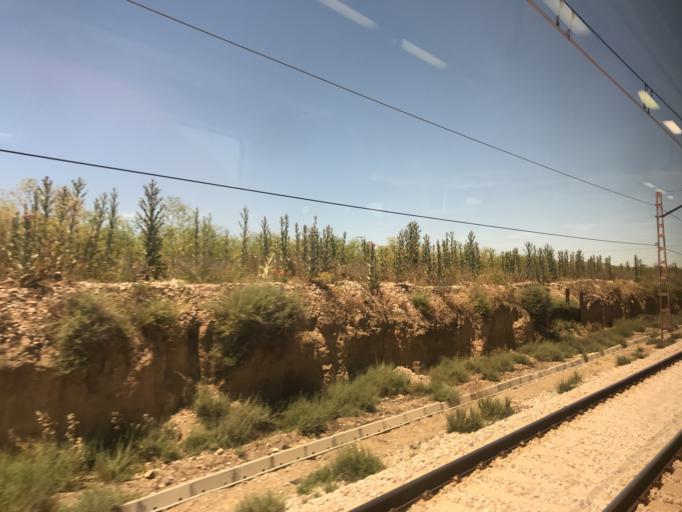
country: ES
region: Madrid
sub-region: Provincia de Madrid
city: Ciempozuelos
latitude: 40.1028
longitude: -3.6259
